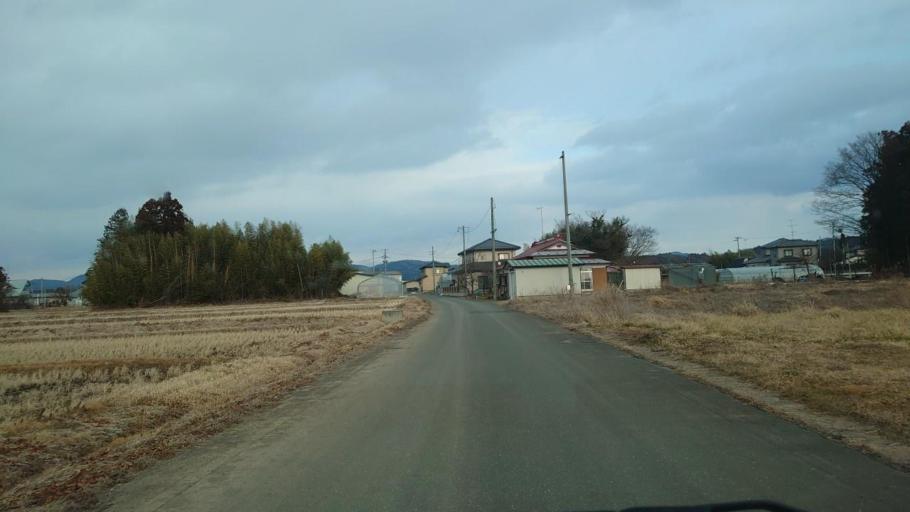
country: JP
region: Miyagi
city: Wakuya
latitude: 38.7040
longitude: 141.2644
